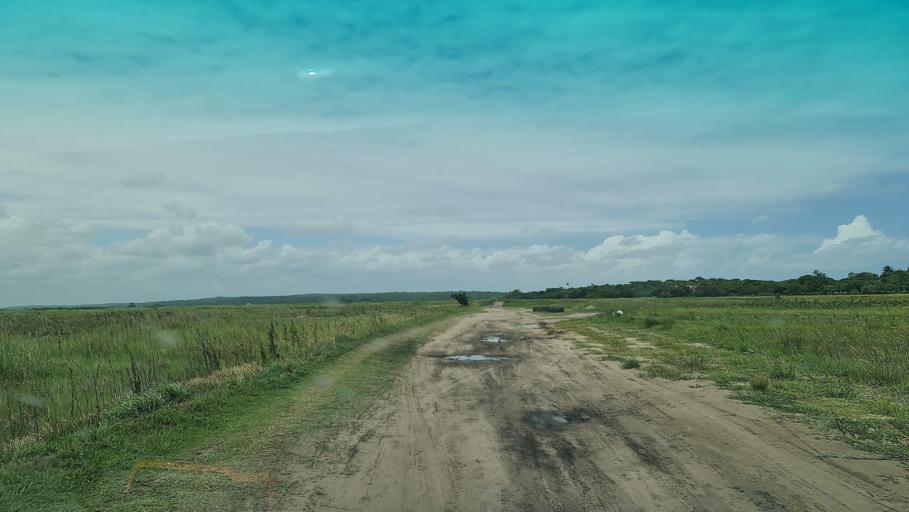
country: MZ
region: Maputo
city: Manhica
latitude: -25.5260
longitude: 32.8550
